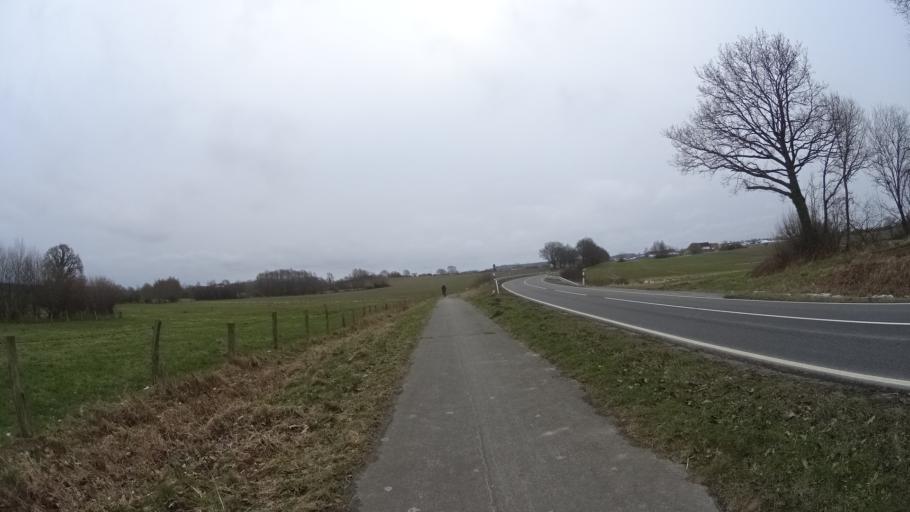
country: DE
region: Schleswig-Holstein
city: Trondel
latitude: 54.3565
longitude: 10.5410
